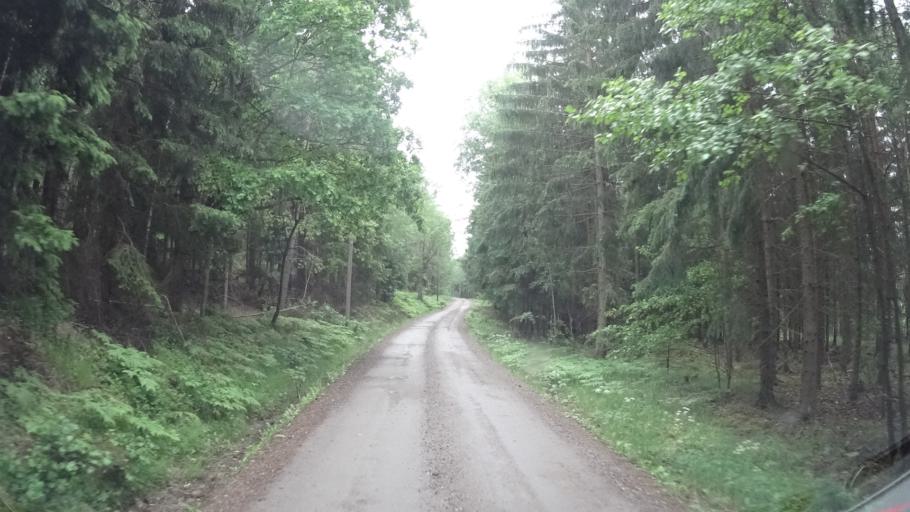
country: SE
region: Soedermanland
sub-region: Nykopings Kommun
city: Olstorp
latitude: 58.7636
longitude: 16.6997
